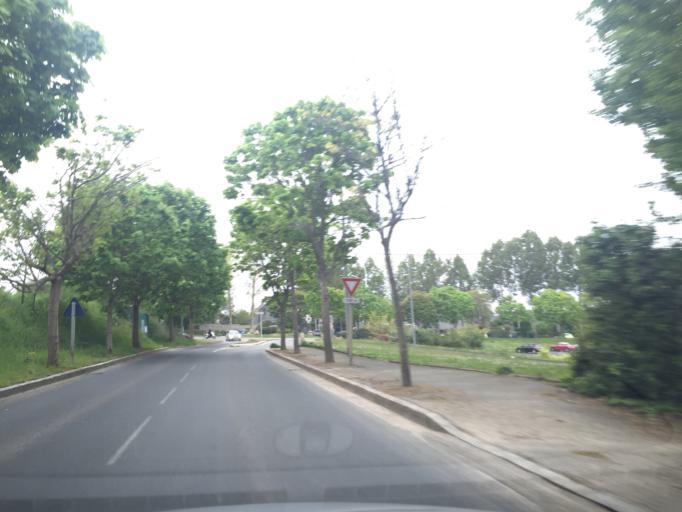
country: FR
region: Brittany
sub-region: Departement des Cotes-d'Armor
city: Paimpol
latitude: 48.7672
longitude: -3.0383
